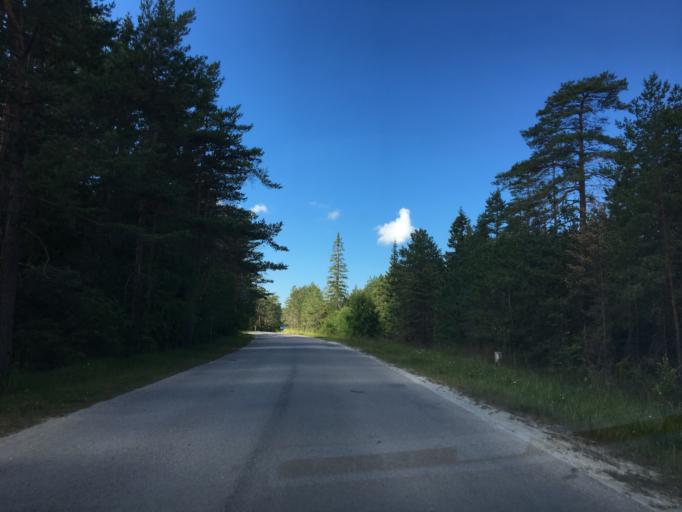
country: EE
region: Harju
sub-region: Nissi vald
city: Riisipere
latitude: 59.2433
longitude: 24.2891
